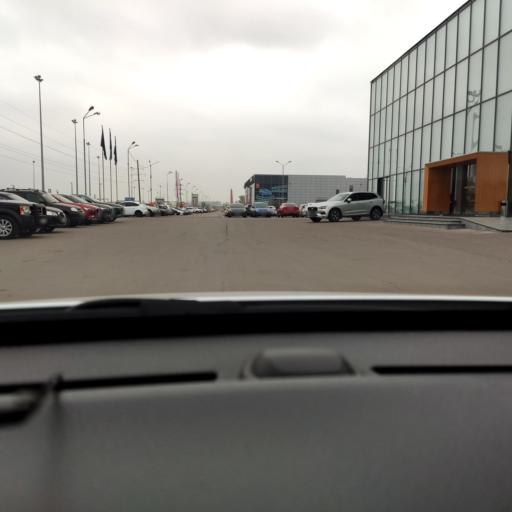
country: RU
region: Voronezj
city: Somovo
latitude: 51.6634
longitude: 39.3004
